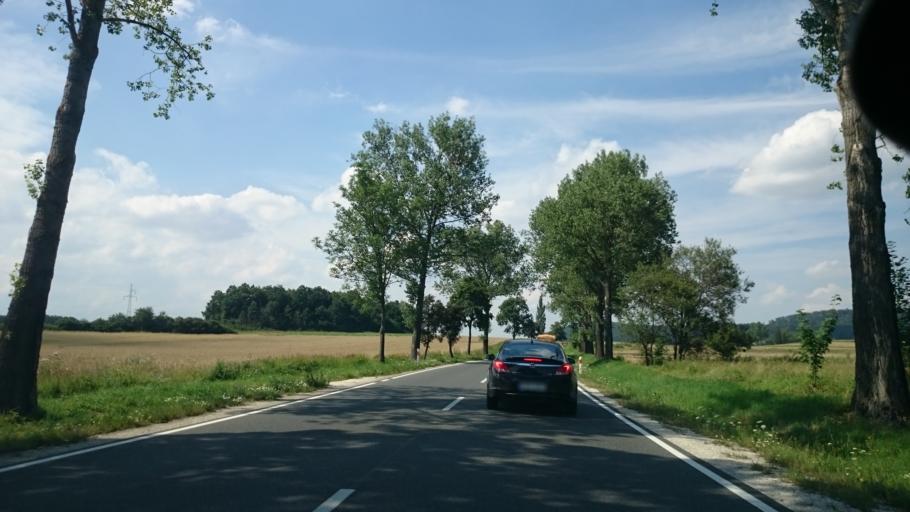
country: PL
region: Lower Silesian Voivodeship
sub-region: Powiat klodzki
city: Bystrzyca Klodzka
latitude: 50.3361
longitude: 16.6633
